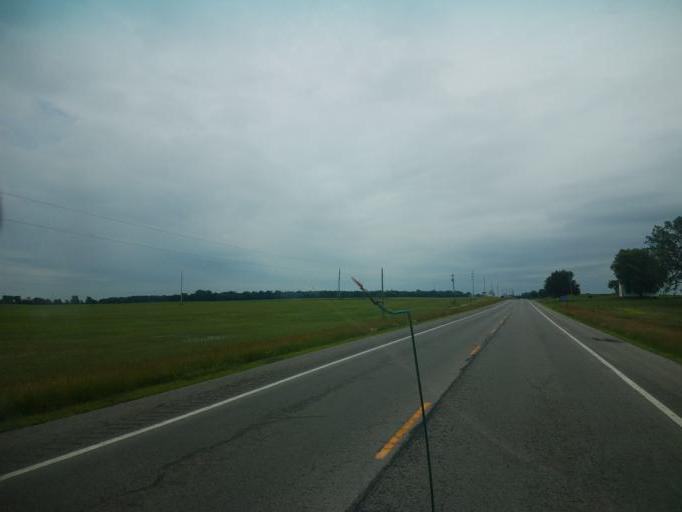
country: US
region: Ohio
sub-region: Hardin County
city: Kenton
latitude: 40.6687
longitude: -83.6580
